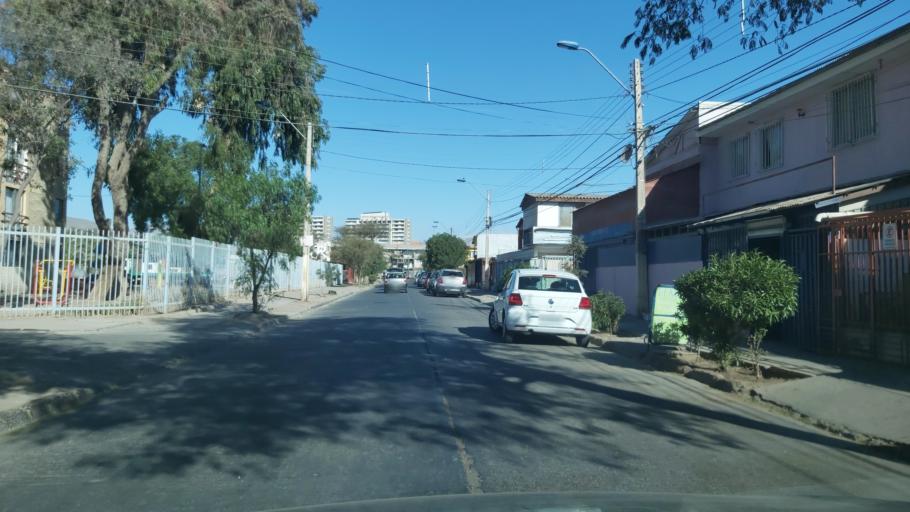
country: CL
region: Atacama
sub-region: Provincia de Copiapo
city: Copiapo
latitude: -27.3753
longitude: -70.3201
